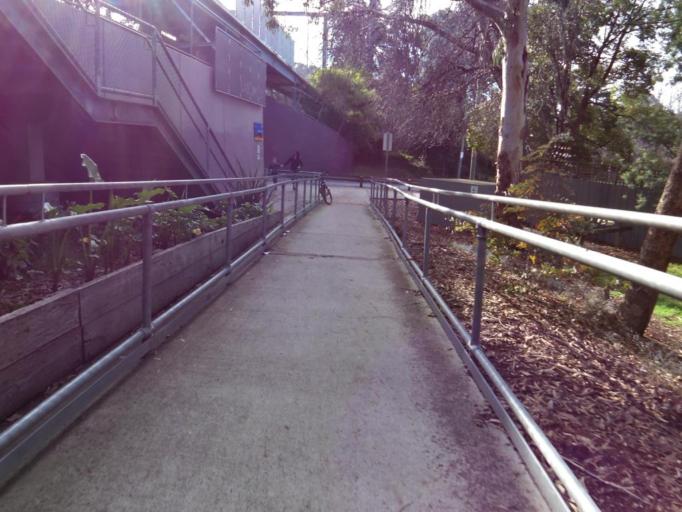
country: AU
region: Victoria
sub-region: Whitehorse
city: Blackburn
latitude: -37.8208
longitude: 145.1410
